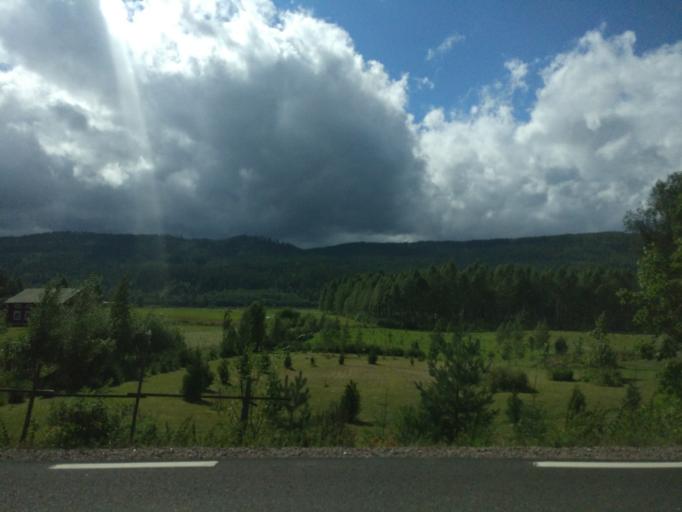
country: SE
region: Vaermland
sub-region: Hagfors Kommun
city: Ekshaerad
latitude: 60.3511
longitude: 13.3371
